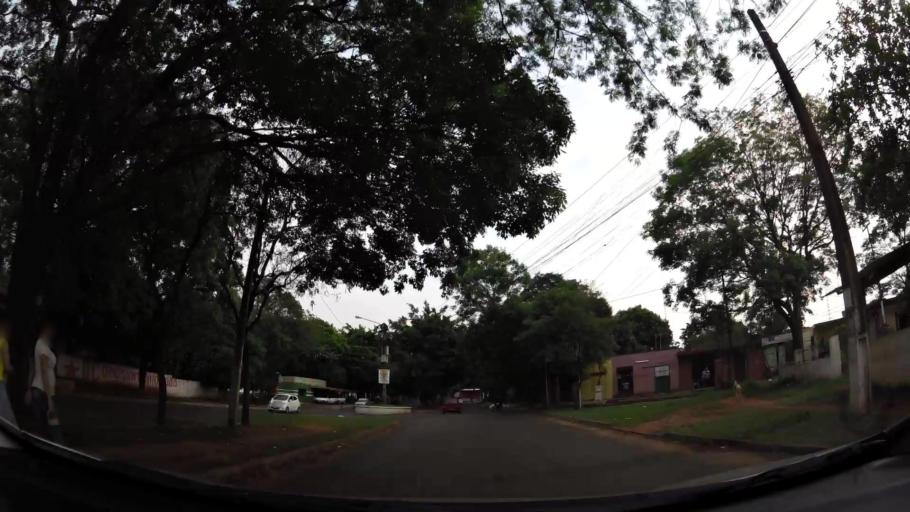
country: PY
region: Alto Parana
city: Presidente Franco
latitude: -25.5400
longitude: -54.6036
